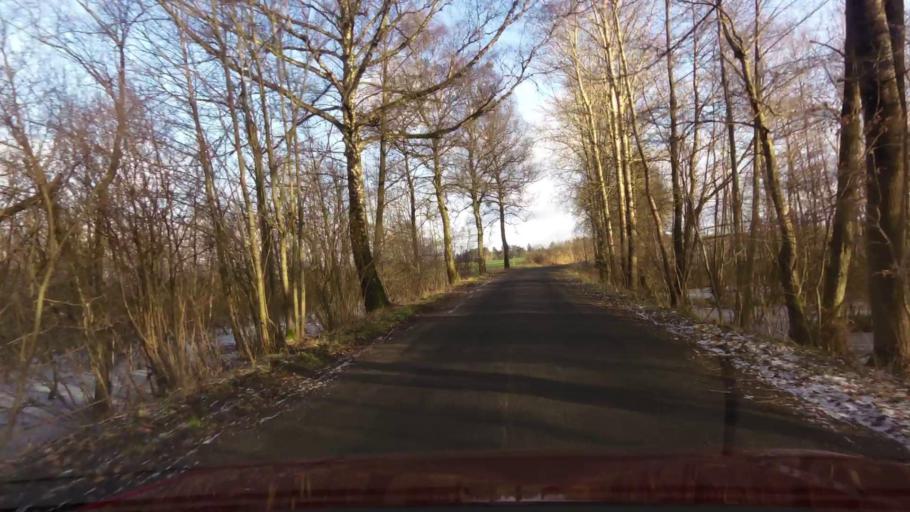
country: PL
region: West Pomeranian Voivodeship
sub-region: Koszalin
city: Koszalin
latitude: 54.0727
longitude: 16.1406
